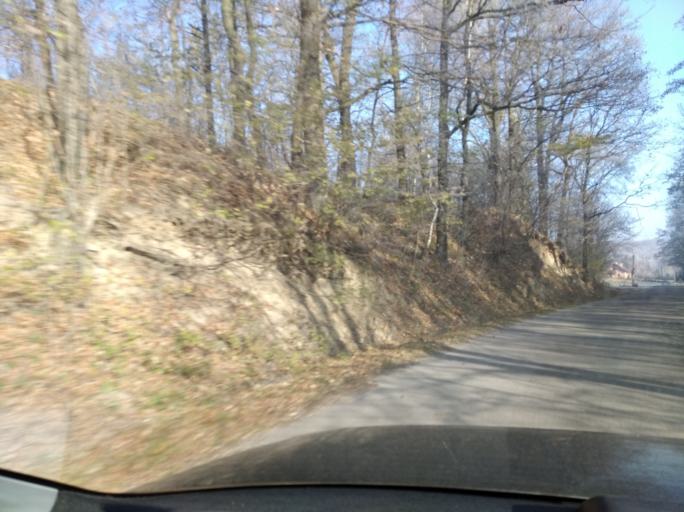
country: PL
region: Subcarpathian Voivodeship
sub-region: Powiat strzyzowski
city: Wysoka Strzyzowska
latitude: 49.8386
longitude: 21.7319
